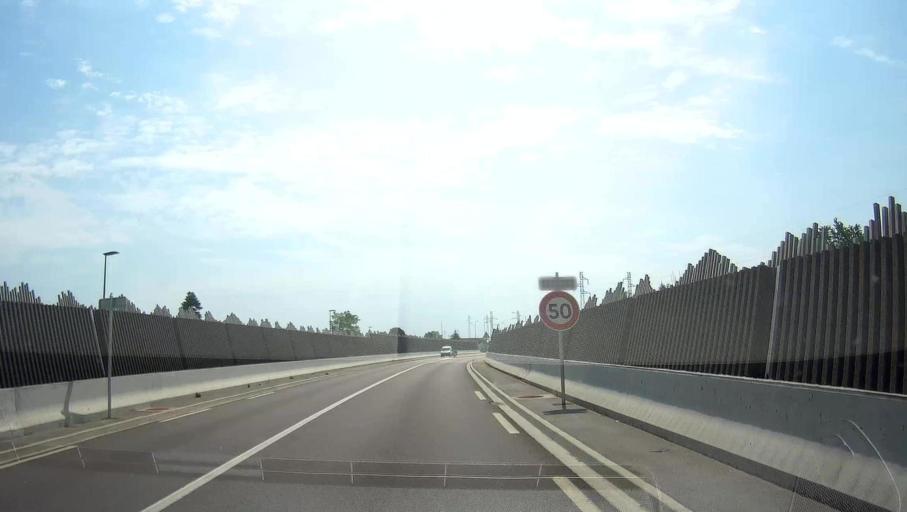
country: FR
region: Bourgogne
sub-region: Departement de la Cote-d'Or
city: Beaune
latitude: 47.0296
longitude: 4.8592
